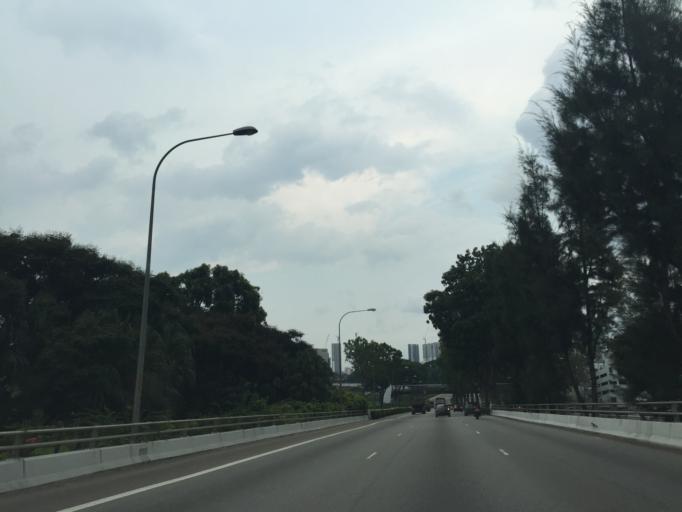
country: SG
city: Singapore
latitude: 1.3233
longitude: 103.7465
